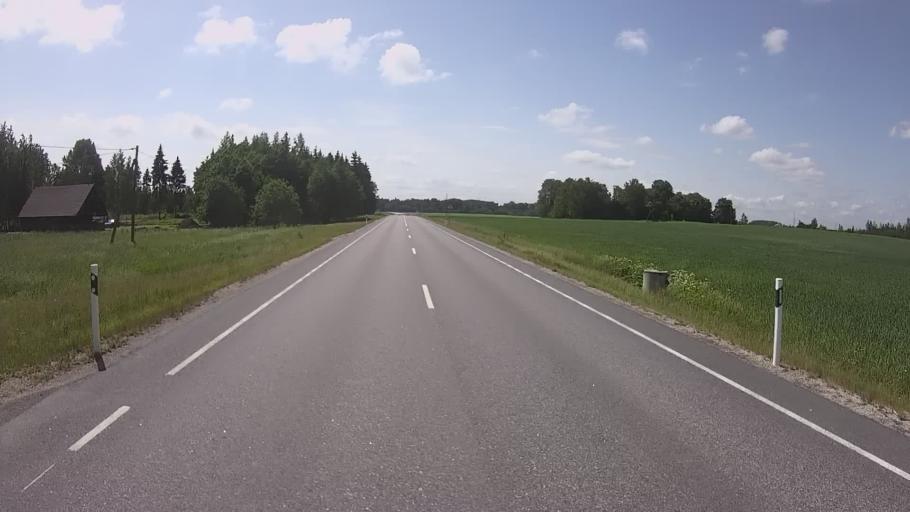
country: EE
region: Tartu
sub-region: Tartu linn
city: Tartu
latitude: 58.3812
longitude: 26.8865
